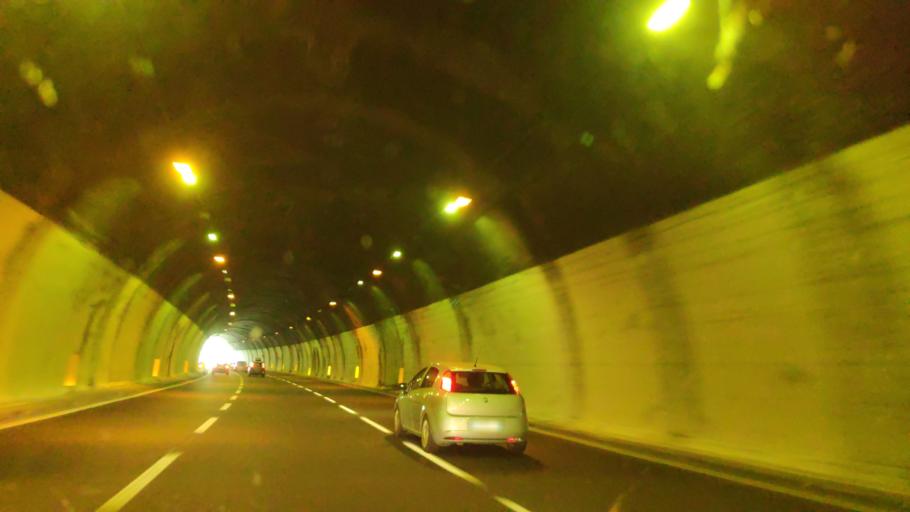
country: IT
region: Campania
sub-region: Provincia di Salerno
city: Piazza del Galdo-Sant'Angelo
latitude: 40.7725
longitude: 14.7157
